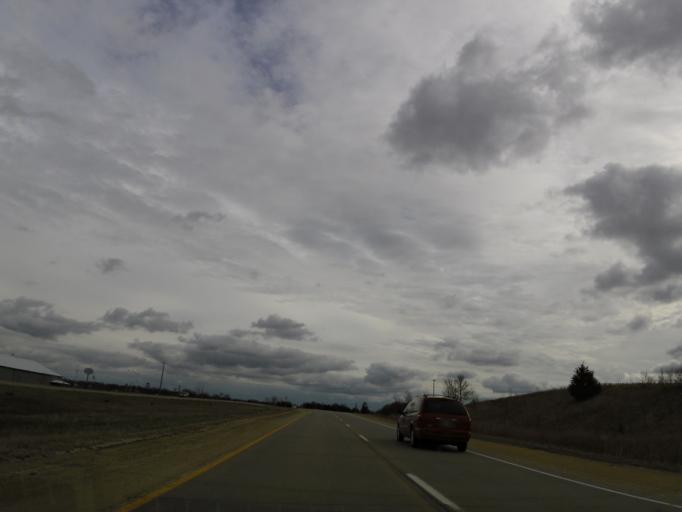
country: US
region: Iowa
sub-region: Bremer County
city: Denver
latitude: 42.6877
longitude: -92.3377
